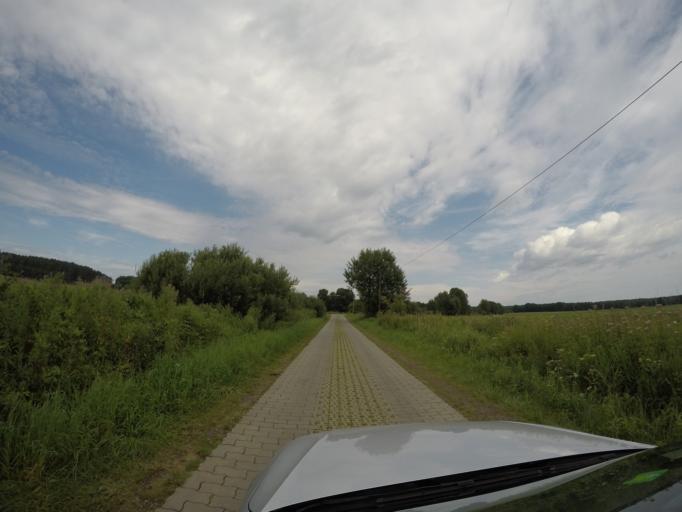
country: DE
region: Mecklenburg-Vorpommern
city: Wesenberg
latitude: 53.3920
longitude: 12.8936
